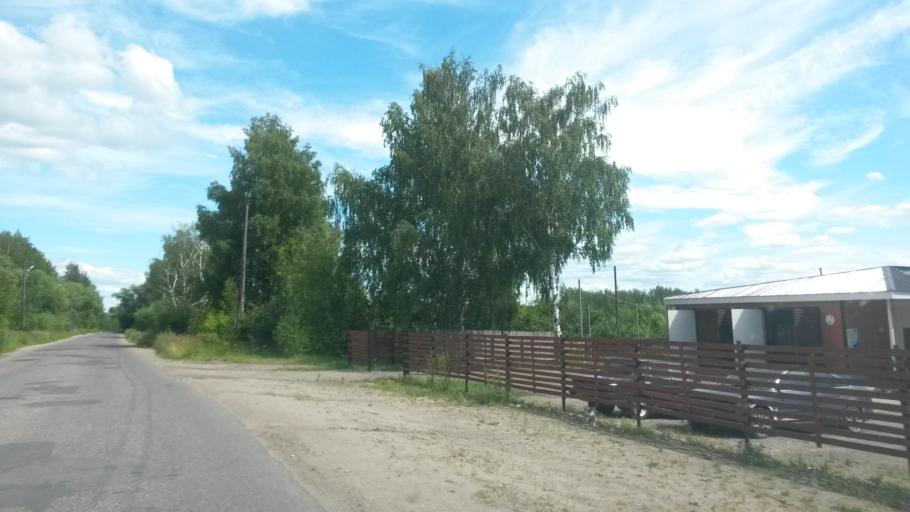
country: RU
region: Ivanovo
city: Zavolzhsk
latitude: 57.4662
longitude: 42.1642
